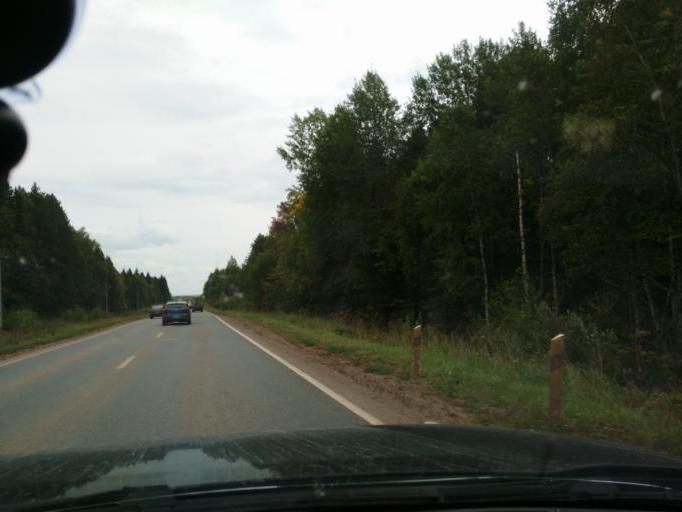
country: RU
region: Perm
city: Chernushka
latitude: 56.5100
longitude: 55.9332
